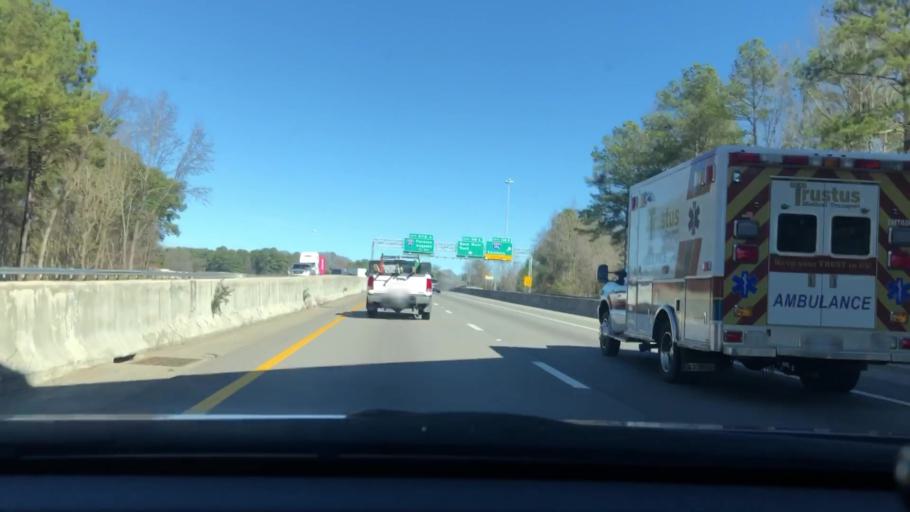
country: US
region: South Carolina
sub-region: Lexington County
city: Saint Andrews
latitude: 34.0260
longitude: -81.1034
